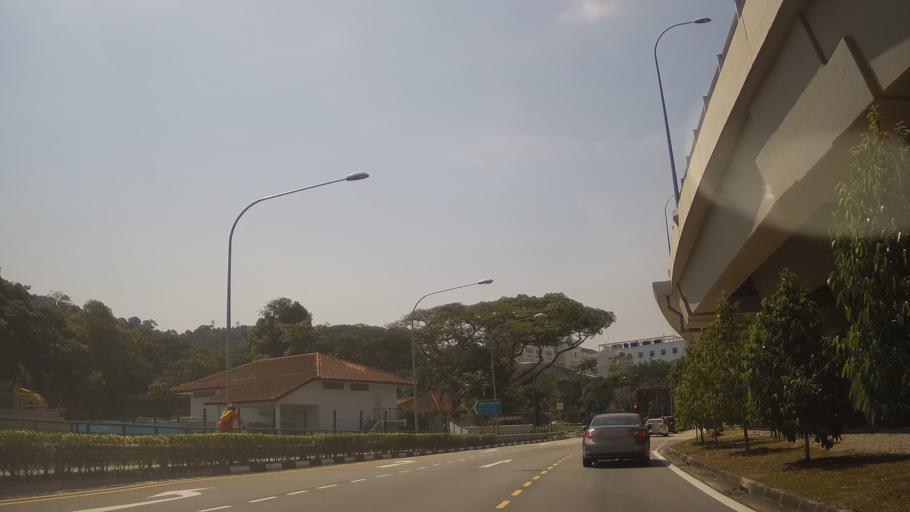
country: MY
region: Johor
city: Johor Bahru
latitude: 1.3645
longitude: 103.7677
